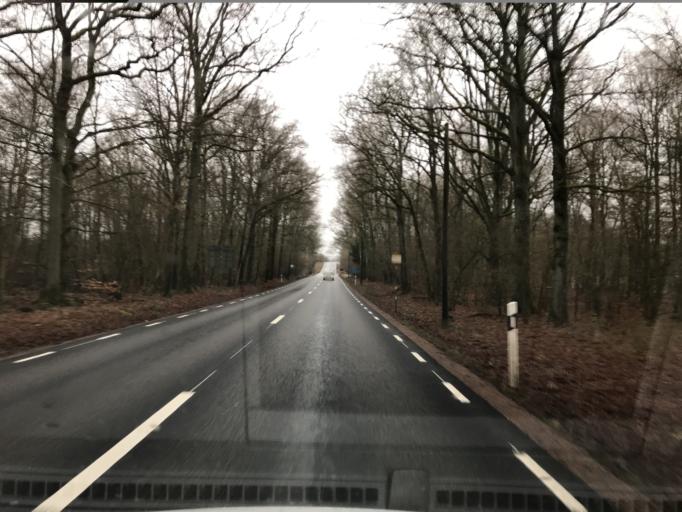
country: SE
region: Skane
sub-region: Klippans Kommun
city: Ljungbyhed
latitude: 56.0484
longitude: 13.2443
